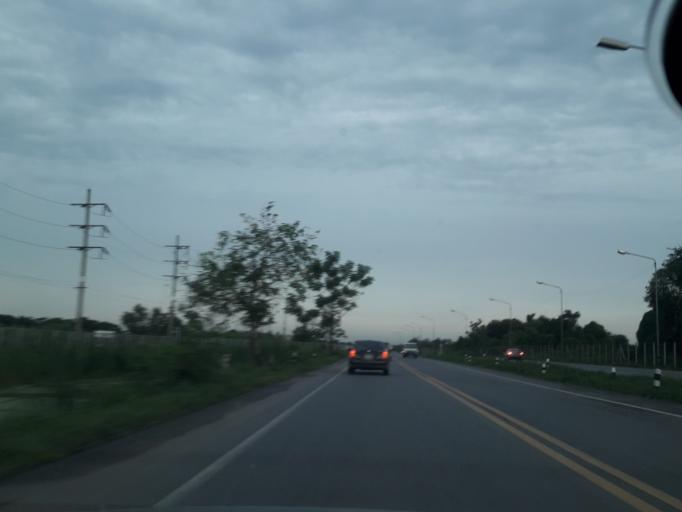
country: TH
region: Pathum Thani
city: Ban Rangsit
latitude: 14.0229
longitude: 100.7488
